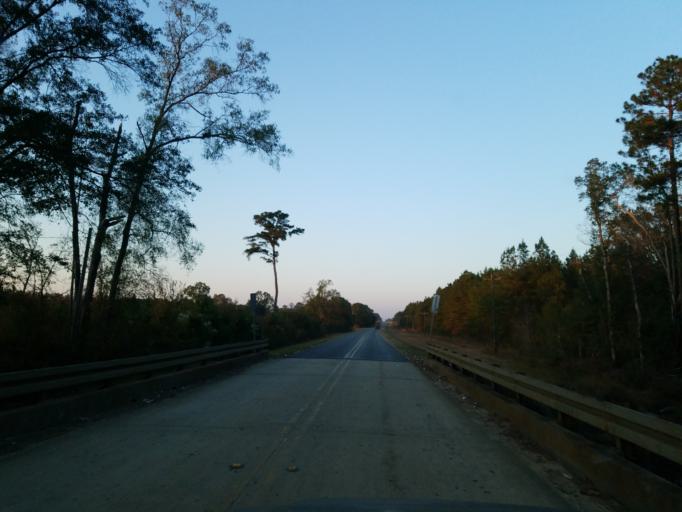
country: US
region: Georgia
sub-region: Ben Hill County
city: Fitzgerald
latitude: 31.6959
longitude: -83.3852
